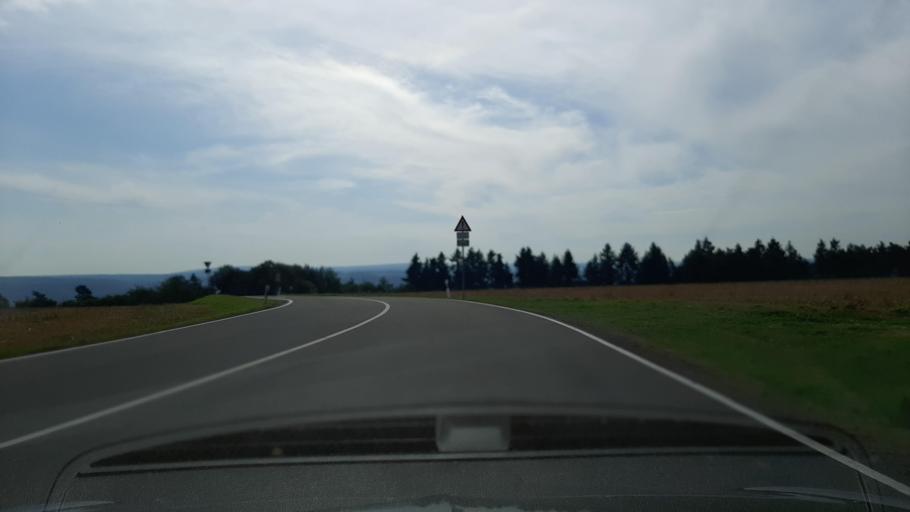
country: DE
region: Rheinland-Pfalz
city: Krov
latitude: 49.9913
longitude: 7.0843
